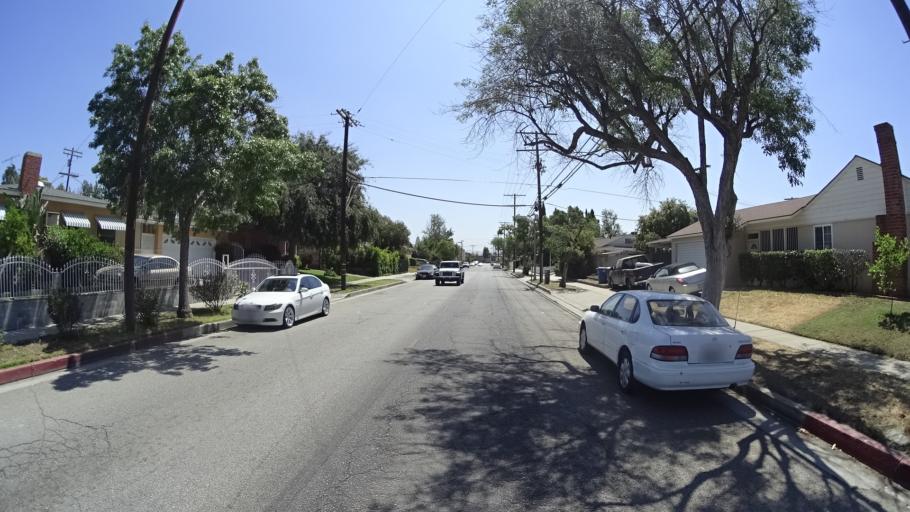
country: US
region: California
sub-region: Los Angeles County
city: Van Nuys
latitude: 34.2296
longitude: -118.4394
